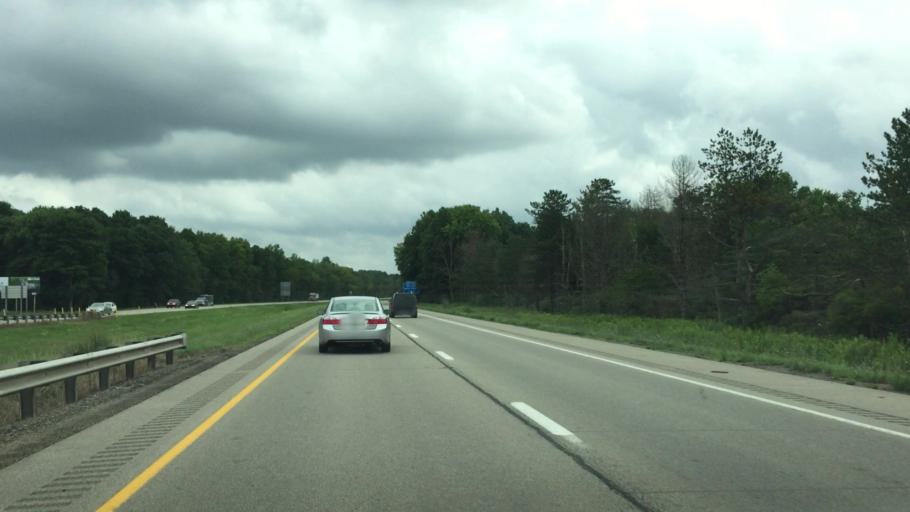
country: US
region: Pennsylvania
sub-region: Mercer County
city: Grove City
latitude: 41.1201
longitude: -80.1487
